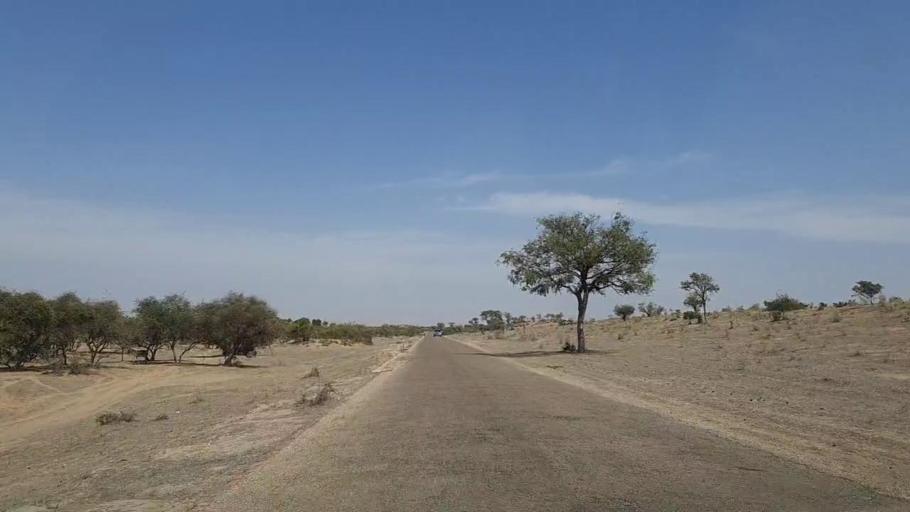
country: PK
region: Sindh
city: Nabisar
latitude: 25.0471
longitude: 69.9585
